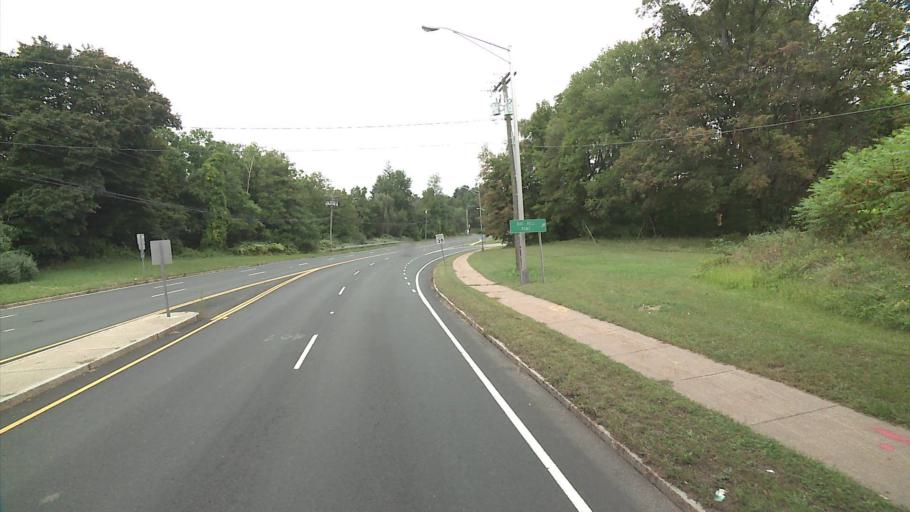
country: US
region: Connecticut
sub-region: Hartford County
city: Windsor
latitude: 41.8754
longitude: -72.6649
